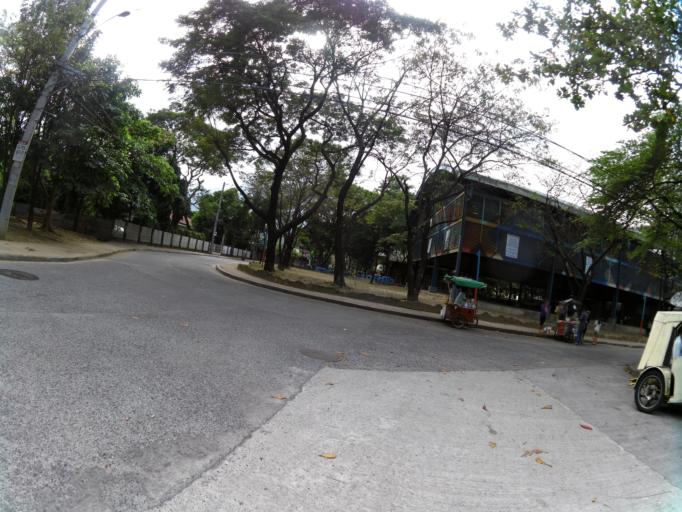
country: PH
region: Metro Manila
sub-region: Marikina
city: Calumpang
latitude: 14.6261
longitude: 121.1039
